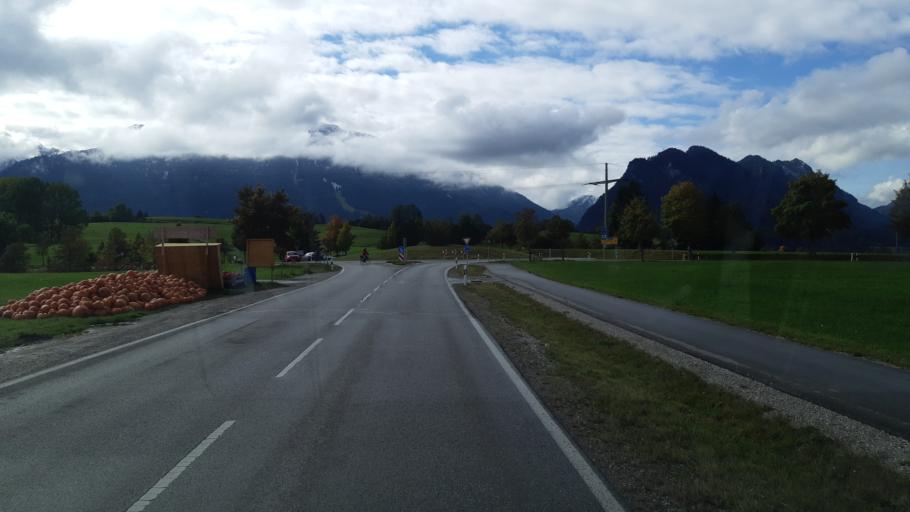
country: DE
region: Bavaria
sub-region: Swabia
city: Pfronten
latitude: 47.5905
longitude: 10.5770
